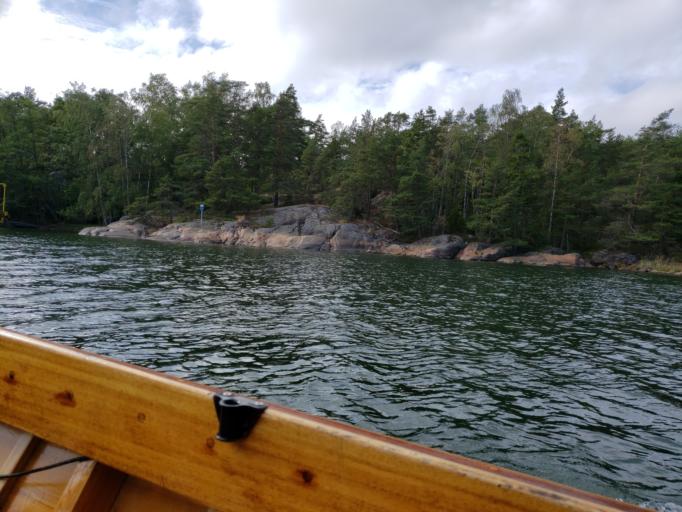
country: FI
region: Varsinais-Suomi
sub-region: Aboland-Turunmaa
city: Dragsfjaerd
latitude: 59.9145
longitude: 22.3796
